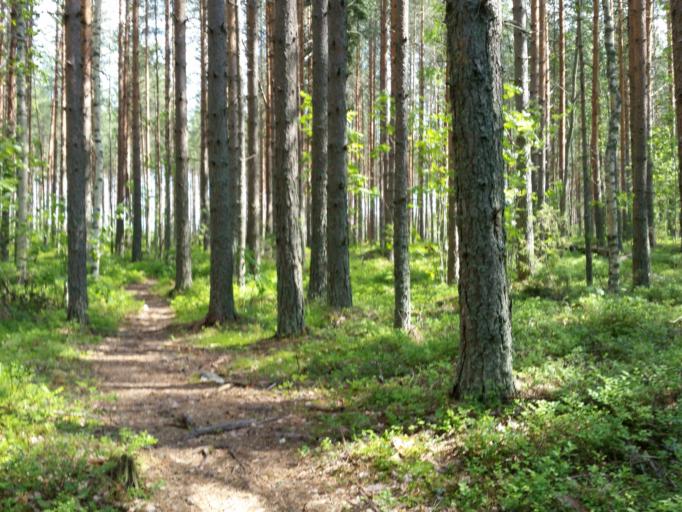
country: FI
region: Northern Savo
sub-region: Ylae-Savo
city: Keitele
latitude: 63.1032
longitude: 26.5296
